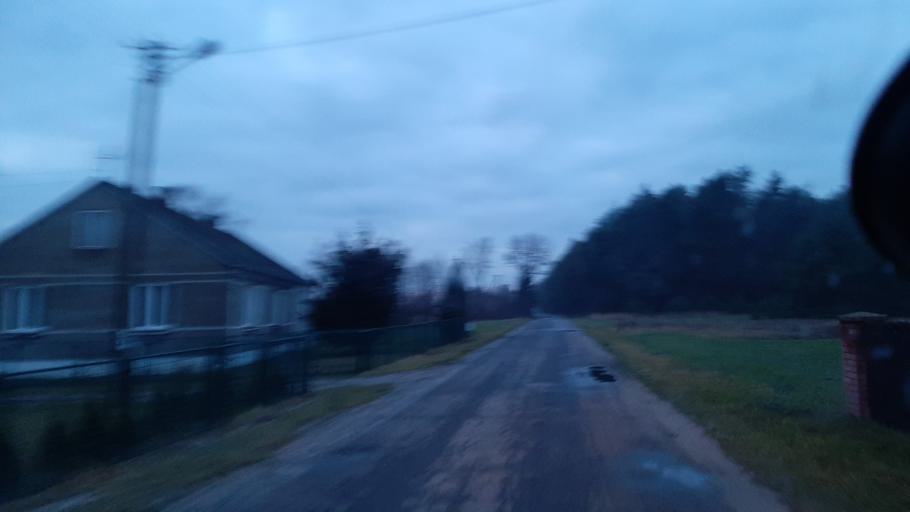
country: PL
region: Lublin Voivodeship
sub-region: Powiat lubartowski
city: Firlej
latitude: 51.5967
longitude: 22.5207
